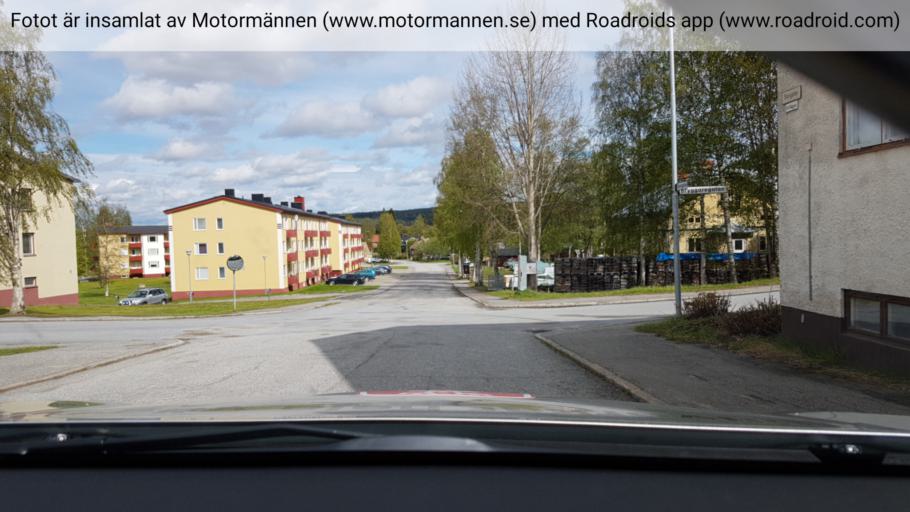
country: SE
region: Vaesterbotten
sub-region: Asele Kommun
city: Asele
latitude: 64.1616
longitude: 17.3580
